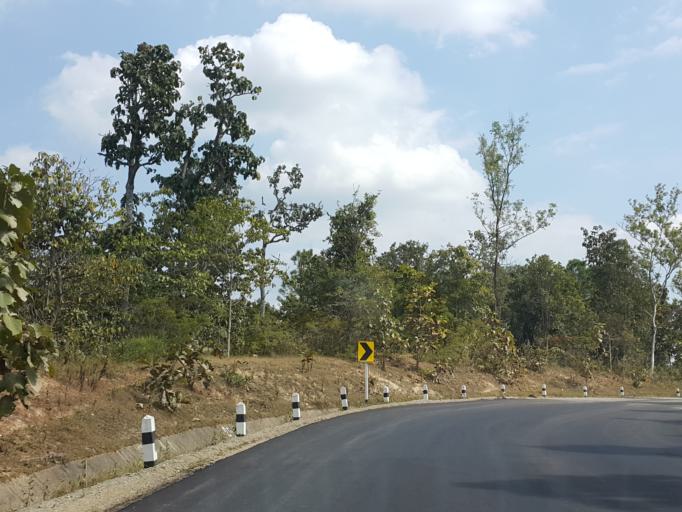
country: TH
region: Chiang Mai
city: Om Koi
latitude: 17.8200
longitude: 98.3651
